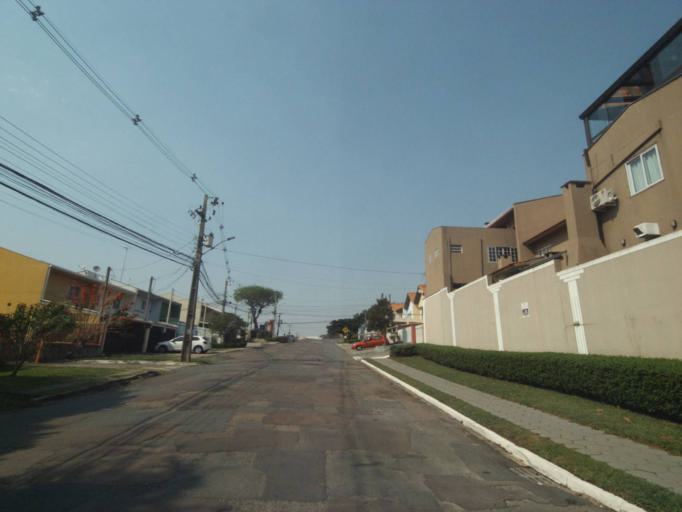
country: BR
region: Parana
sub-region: Sao Jose Dos Pinhais
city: Sao Jose dos Pinhais
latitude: -25.5221
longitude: -49.2496
